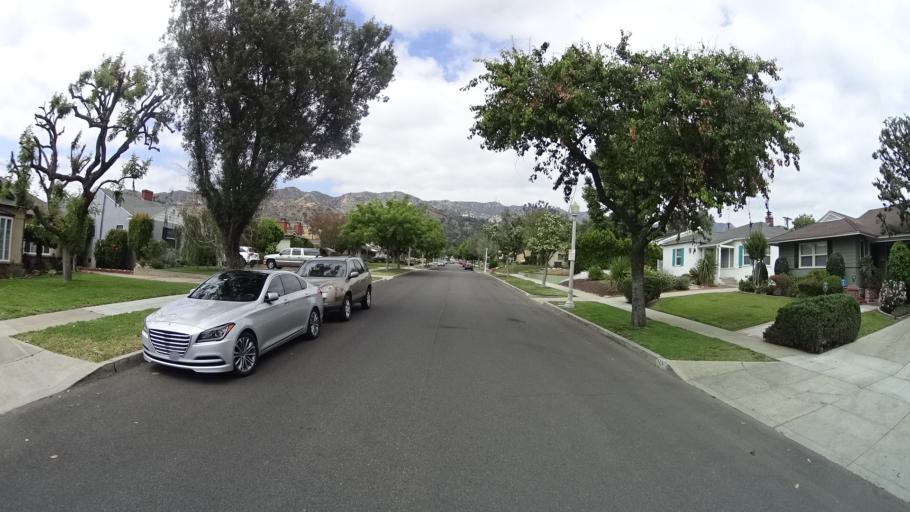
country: US
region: California
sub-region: Los Angeles County
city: Burbank
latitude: 34.1954
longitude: -118.3213
